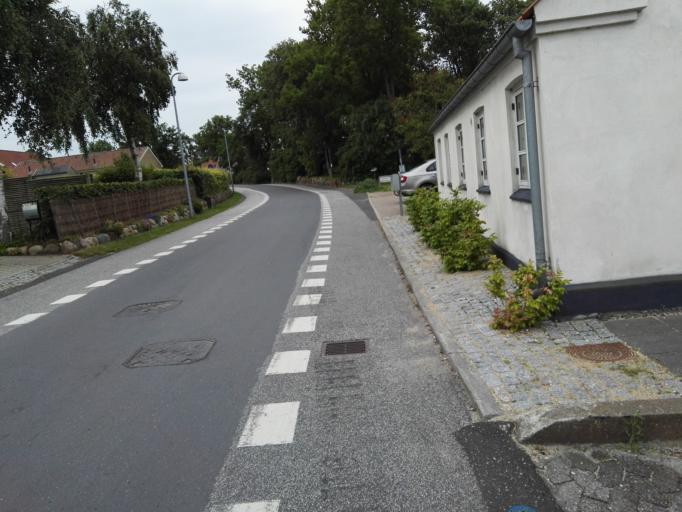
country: DK
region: Zealand
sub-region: Roskilde Kommune
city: Jyllinge
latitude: 55.7498
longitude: 12.1024
